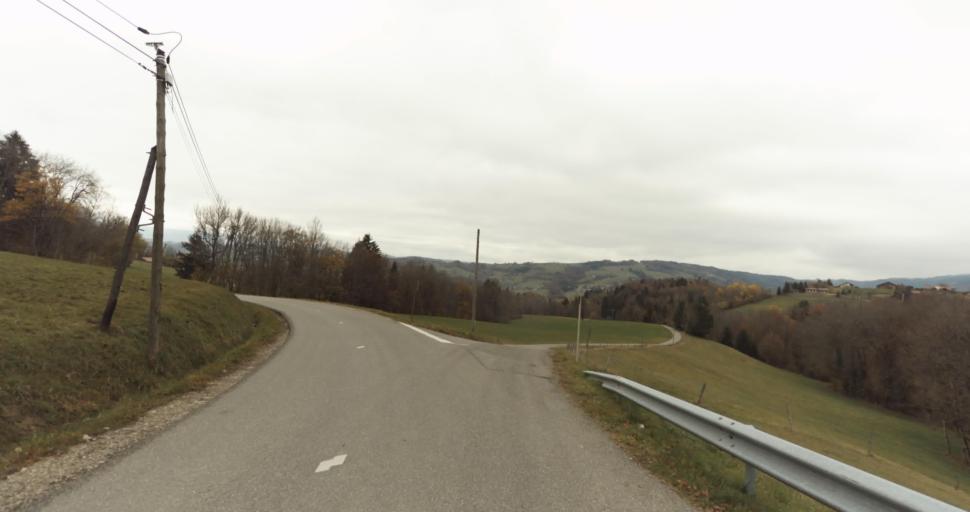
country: FR
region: Rhone-Alpes
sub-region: Departement de la Haute-Savoie
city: Thorens-Glieres
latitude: 45.9803
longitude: 6.2228
